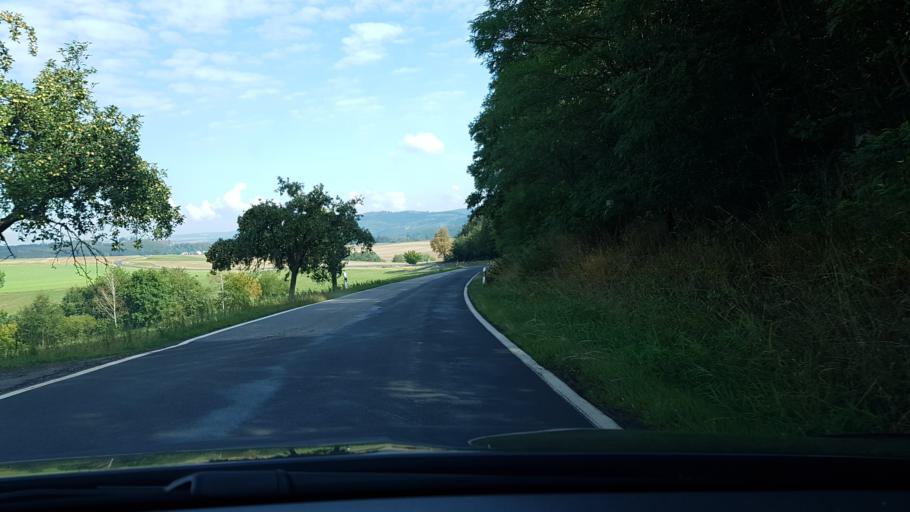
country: DE
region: Rheinland-Pfalz
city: Morshausen
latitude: 50.1943
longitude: 7.4413
